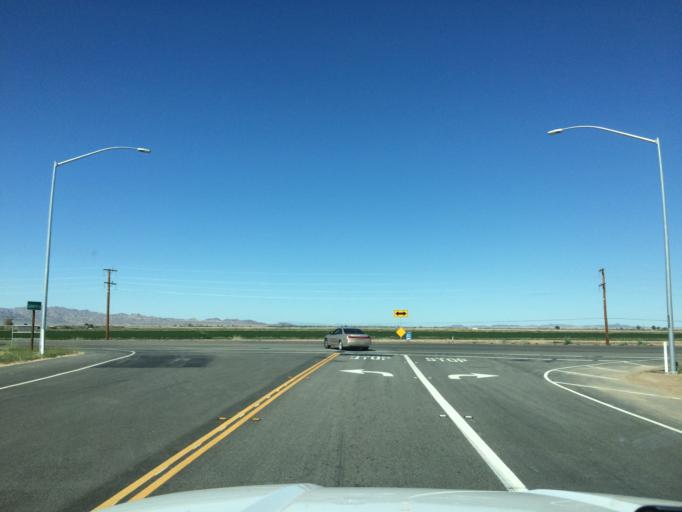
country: US
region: Arizona
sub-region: La Paz County
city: Ehrenberg
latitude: 33.6093
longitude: -114.5482
